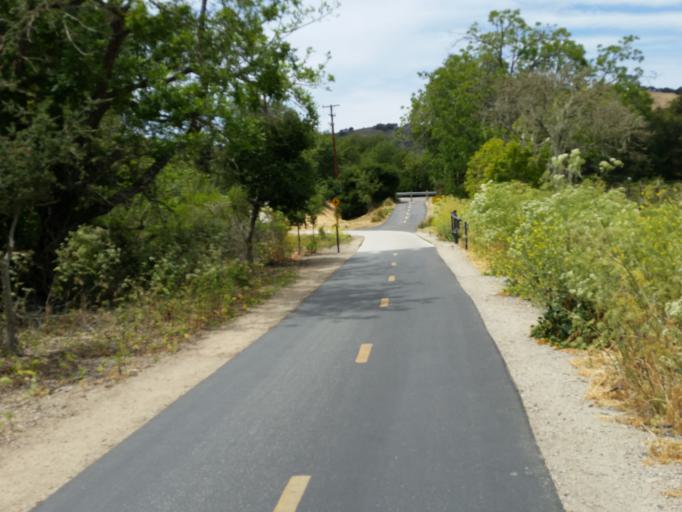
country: US
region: California
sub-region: San Luis Obispo County
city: Avila Beach
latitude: 35.1887
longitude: -120.7179
